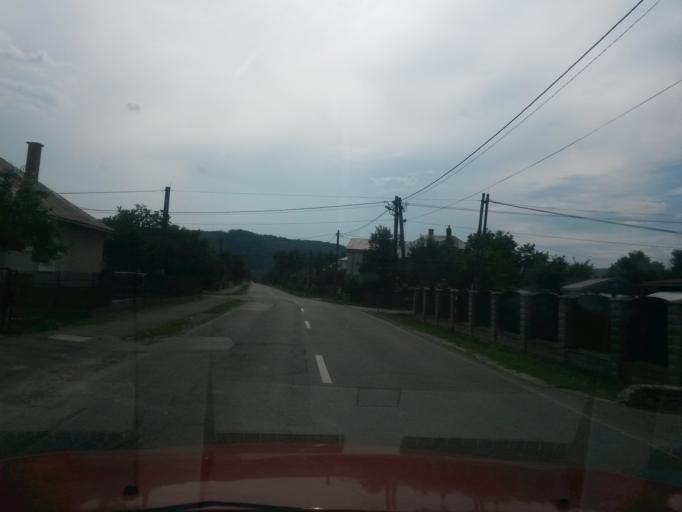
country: SK
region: Presovsky
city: Humenne
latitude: 48.9737
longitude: 21.9626
